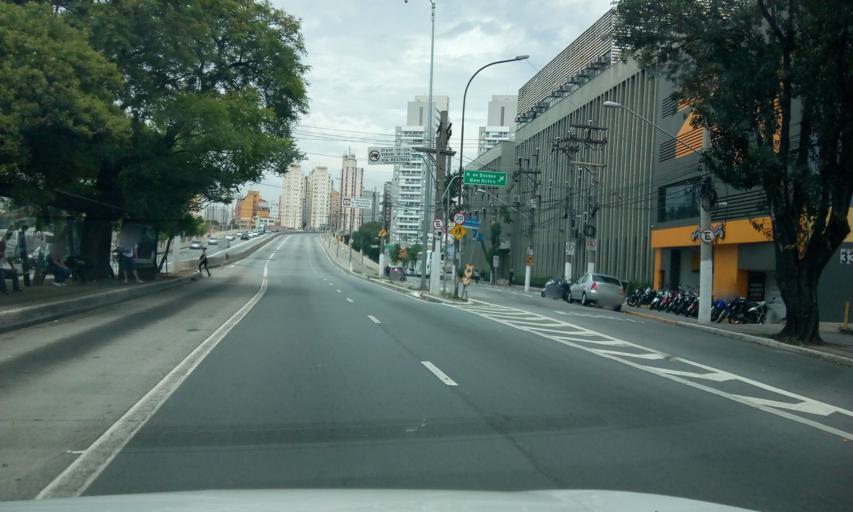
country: BR
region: Sao Paulo
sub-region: Sao Paulo
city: Sao Paulo
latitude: -23.5248
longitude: -46.6497
